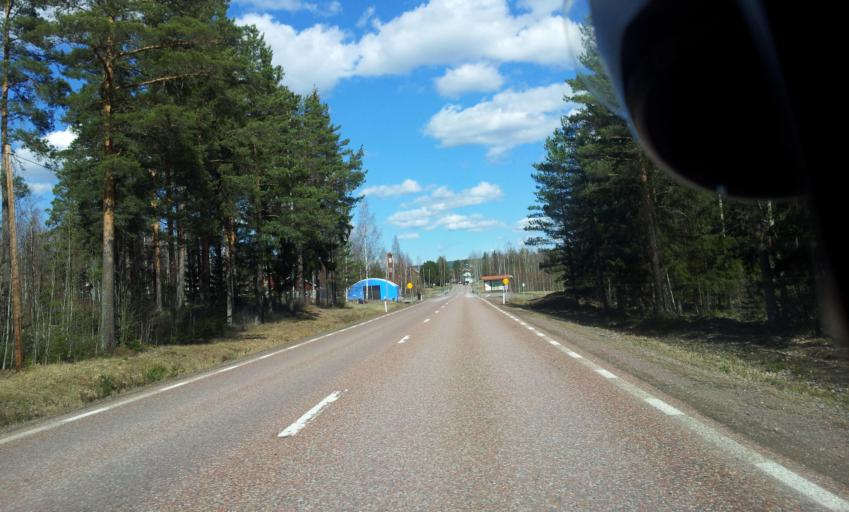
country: SE
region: Dalarna
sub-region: Faluns Kommun
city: Svardsjo
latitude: 60.8020
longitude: 15.7529
